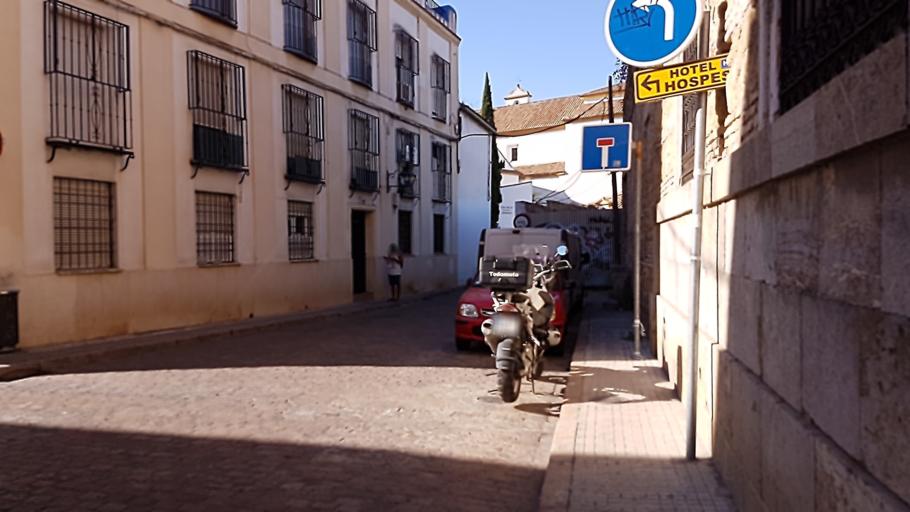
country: ES
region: Andalusia
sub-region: Province of Cordoba
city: Cordoba
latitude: 37.8867
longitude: -4.7764
